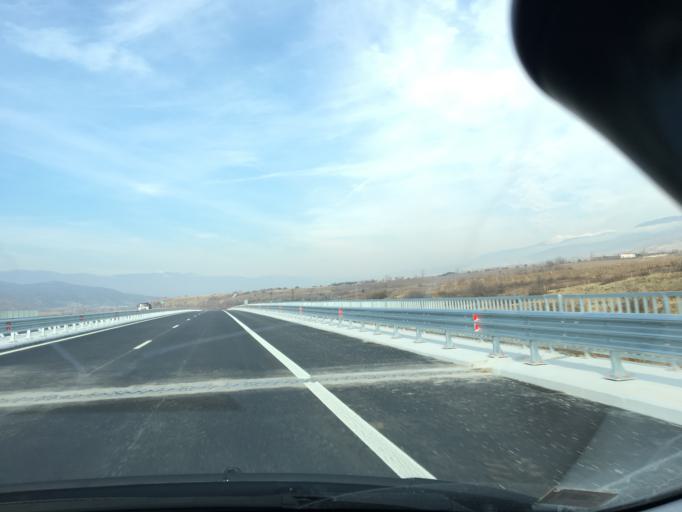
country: BG
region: Blagoevgrad
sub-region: Obshtina Sandanski
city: Sandanski
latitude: 41.5476
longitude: 23.2533
